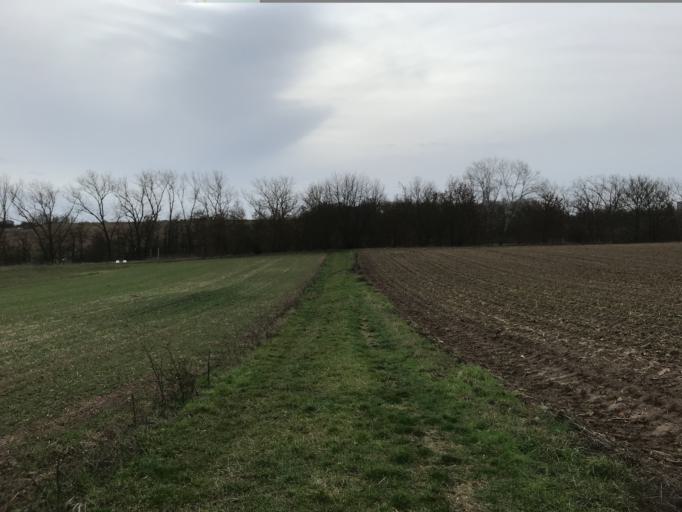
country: DE
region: Rheinland-Pfalz
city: Klein-Winternheim
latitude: 49.9750
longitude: 8.2093
